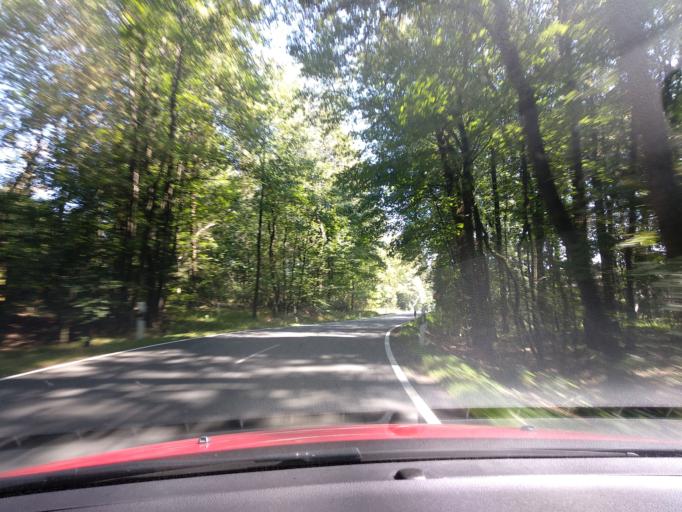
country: DE
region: North Rhine-Westphalia
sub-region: Regierungsbezirk Detmold
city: Bad Driburg
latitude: 51.6780
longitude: 8.9724
